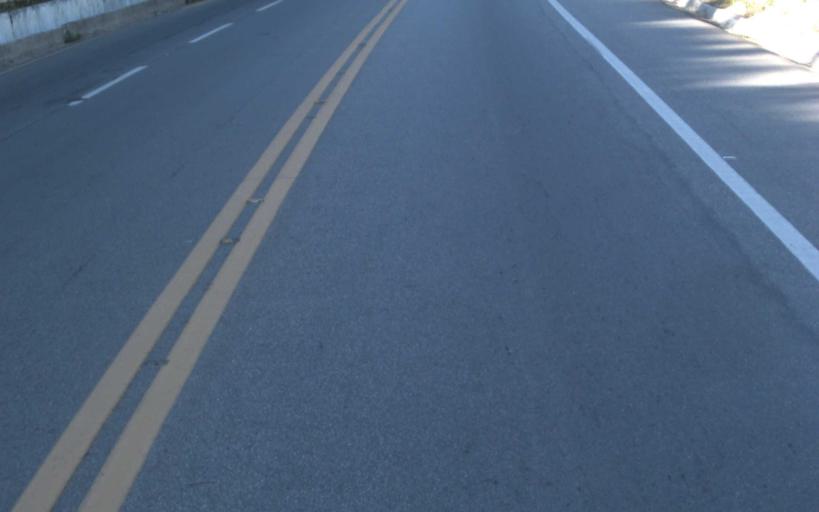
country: BR
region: Minas Gerais
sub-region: Timoteo
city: Timoteo
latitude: -19.6209
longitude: -42.8026
